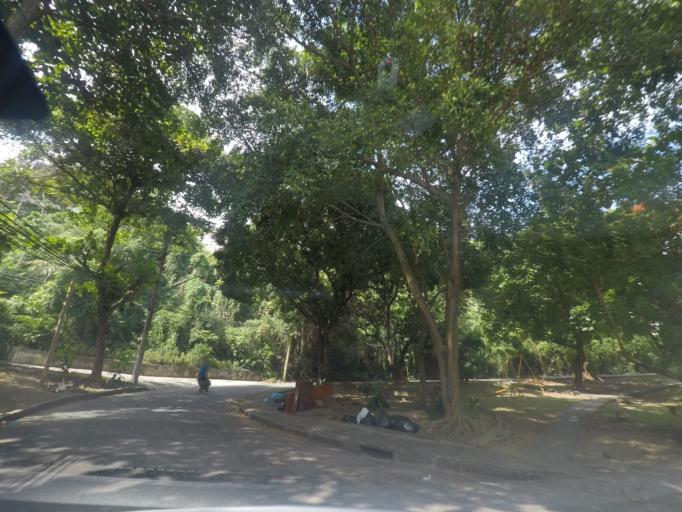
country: BR
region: Rio de Janeiro
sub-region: Rio De Janeiro
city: Rio de Janeiro
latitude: -22.8150
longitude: -43.1973
